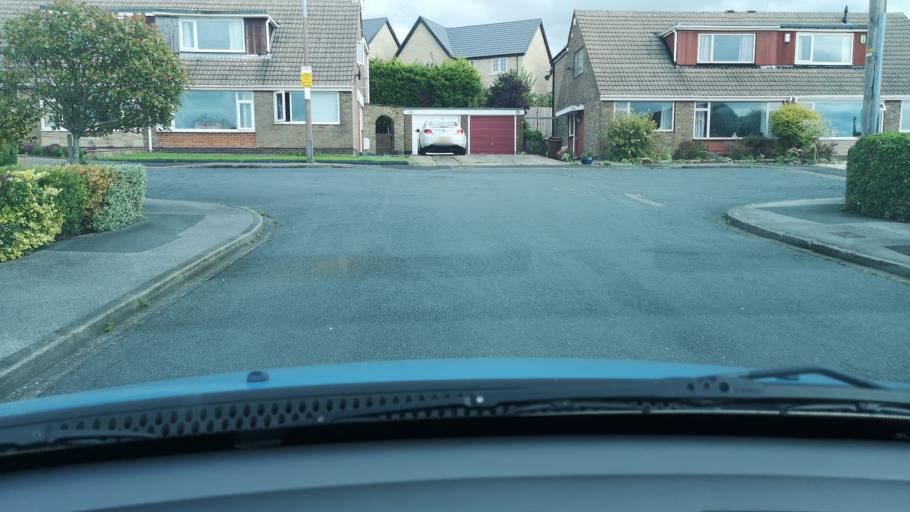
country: GB
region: England
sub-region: City and Borough of Leeds
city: Drighlington
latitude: 53.7357
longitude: -1.6494
